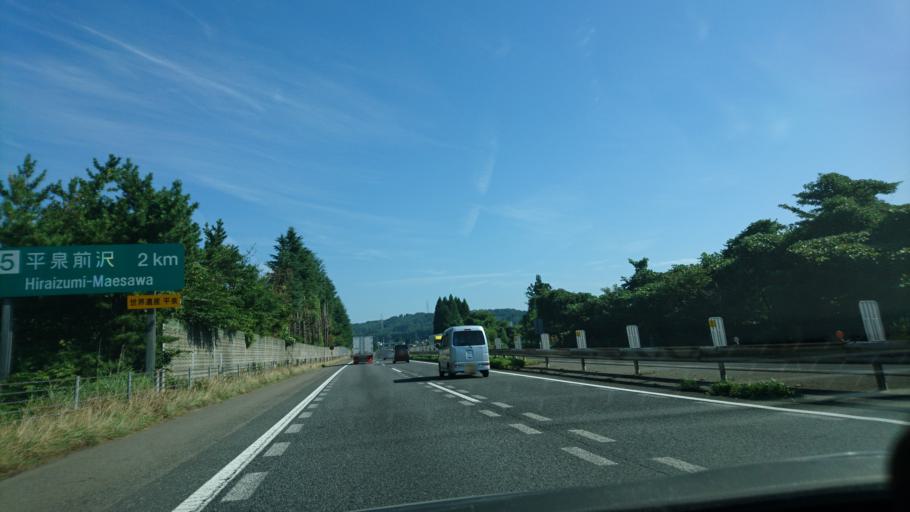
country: JP
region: Iwate
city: Ichinoseki
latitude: 39.0094
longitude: 141.0872
